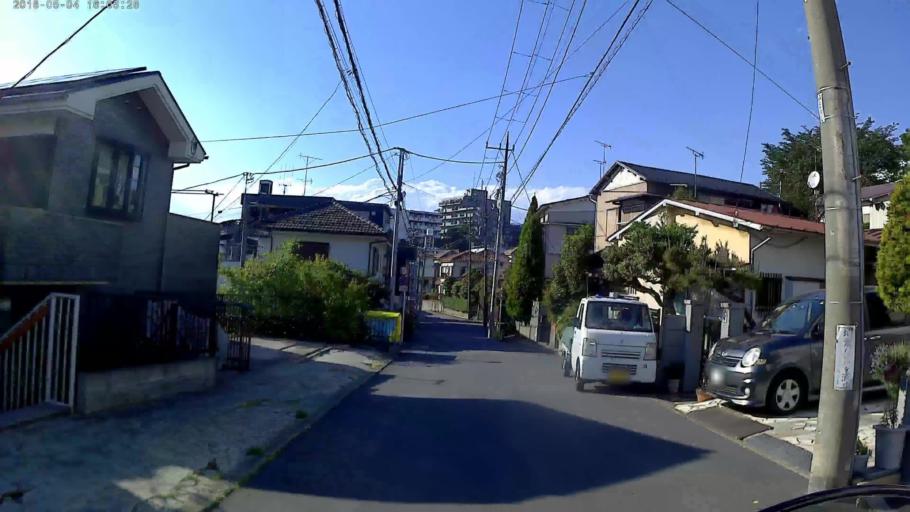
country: JP
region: Kanagawa
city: Yokohama
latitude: 35.4929
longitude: 139.6586
